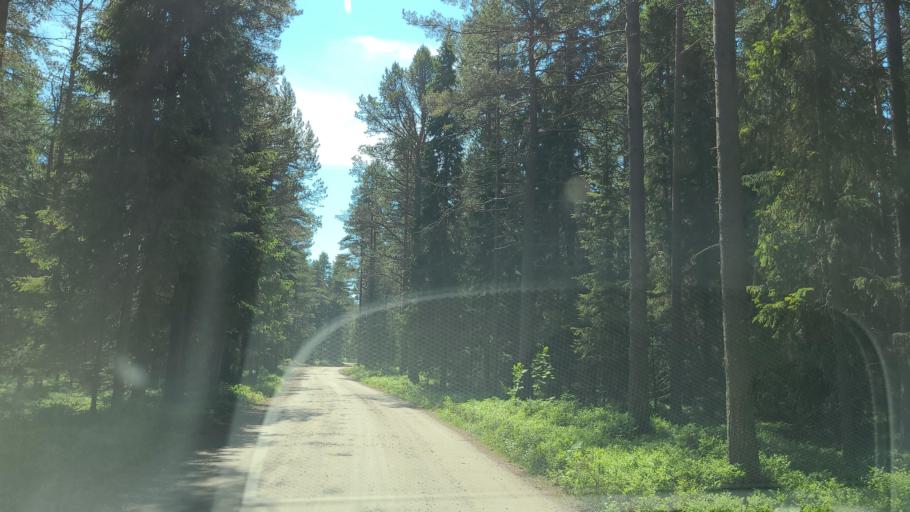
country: SE
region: Vaesterbotten
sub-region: Robertsfors Kommun
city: Robertsfors
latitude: 64.1419
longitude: 20.9603
